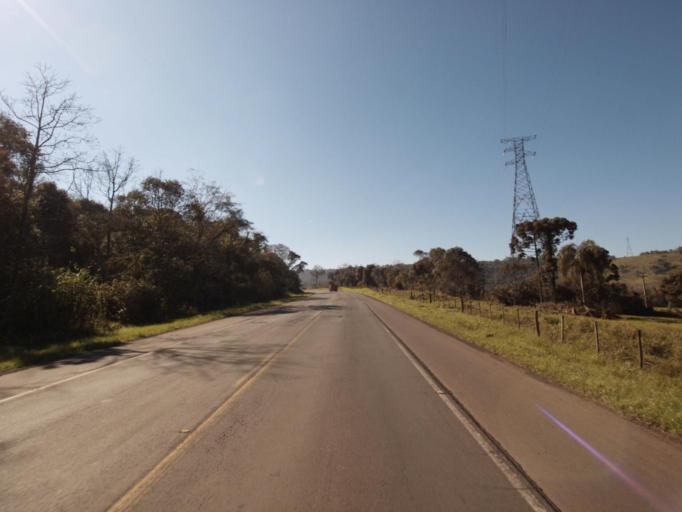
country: BR
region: Rio Grande do Sul
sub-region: Frederico Westphalen
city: Frederico Westphalen
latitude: -27.0663
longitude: -53.2244
